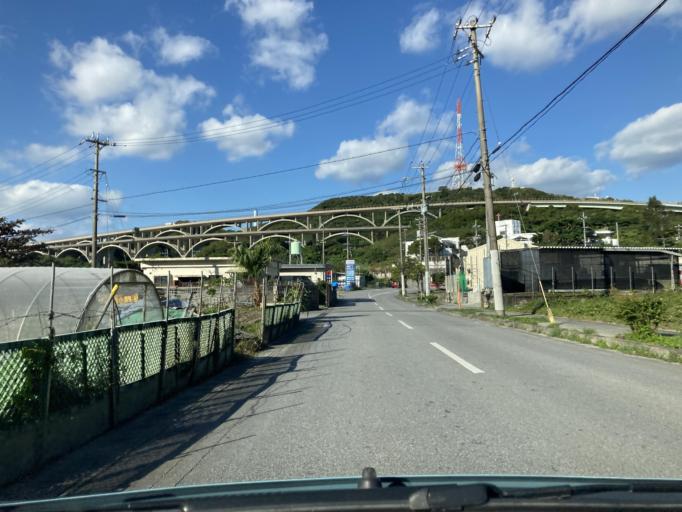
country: JP
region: Okinawa
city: Ginowan
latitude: 26.2156
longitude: 127.7430
